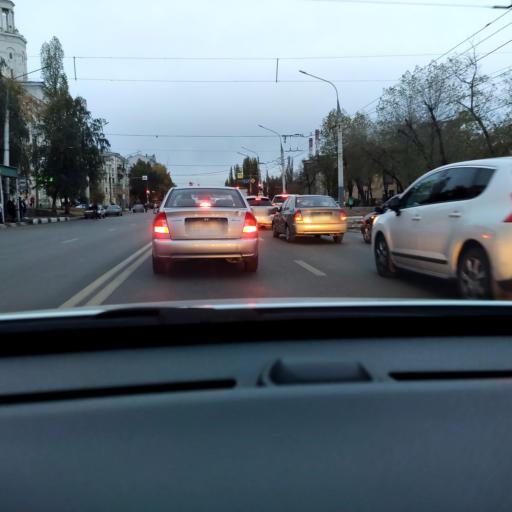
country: RU
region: Voronezj
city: Voronezh
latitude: 51.6347
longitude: 39.2331
